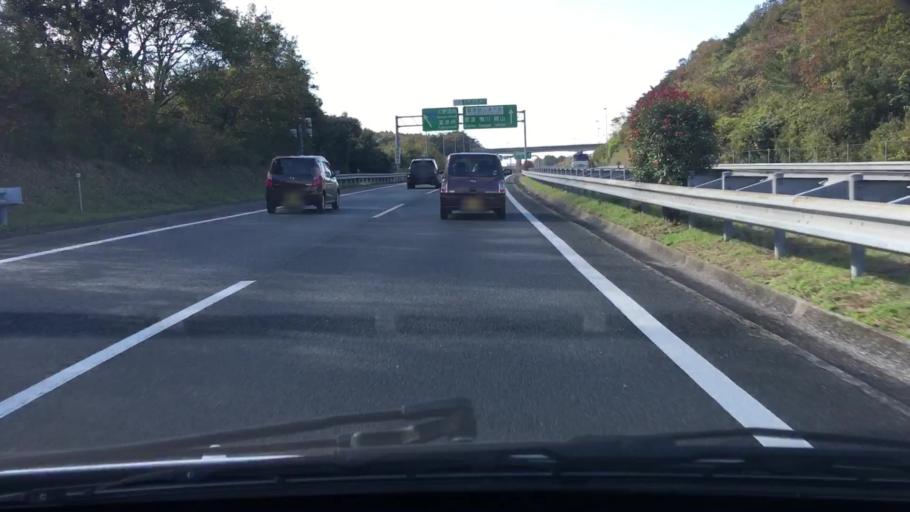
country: JP
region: Chiba
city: Kisarazu
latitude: 35.3581
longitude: 139.9538
